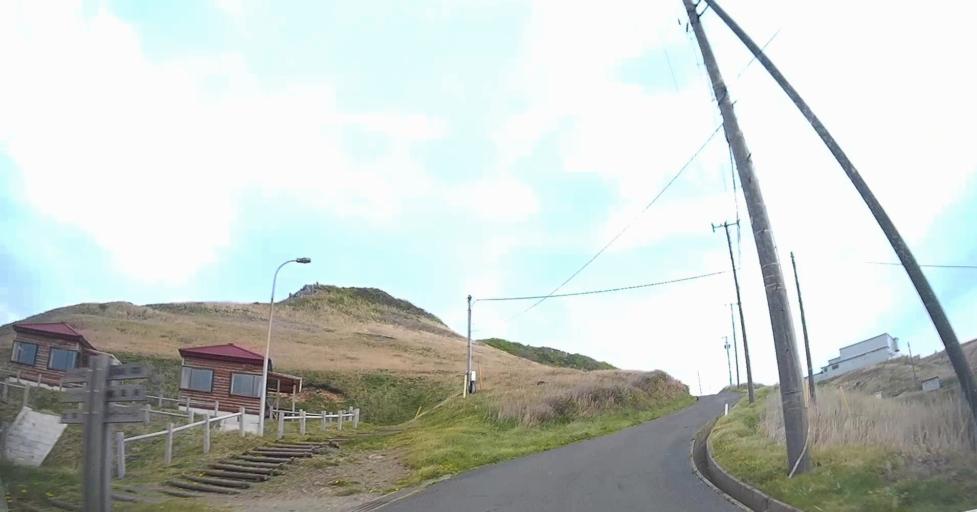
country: JP
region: Aomori
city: Shimokizukuri
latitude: 41.2530
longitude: 140.3426
